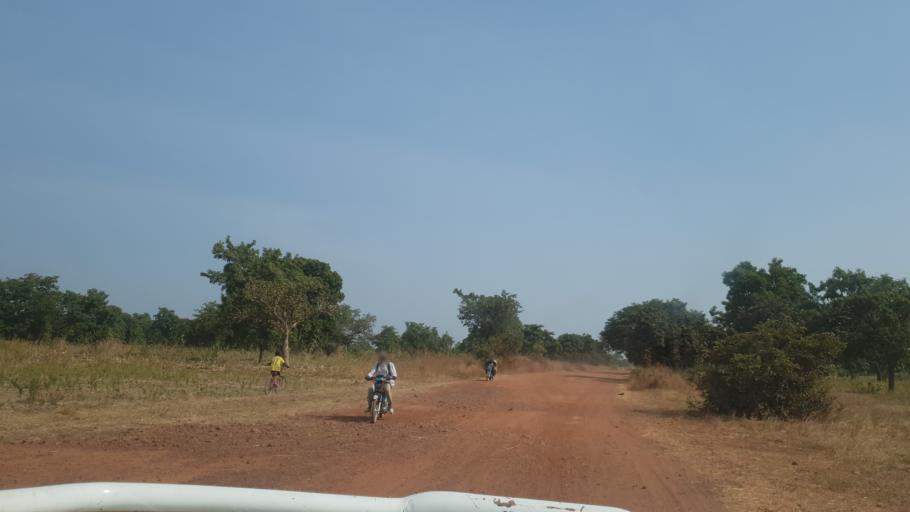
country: ML
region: Koulikoro
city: Dioila
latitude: 12.2276
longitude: -6.2169
